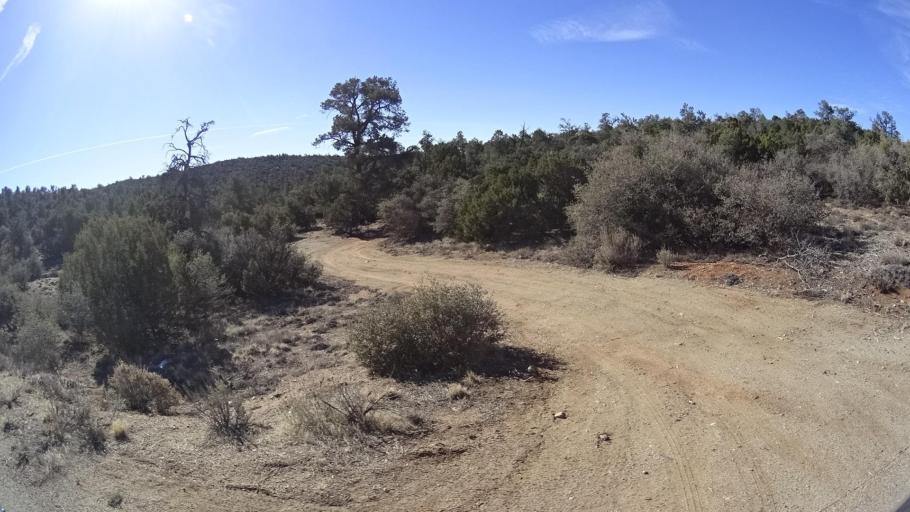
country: US
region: California
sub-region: Kern County
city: Pine Mountain Club
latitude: 34.8721
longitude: -119.2696
